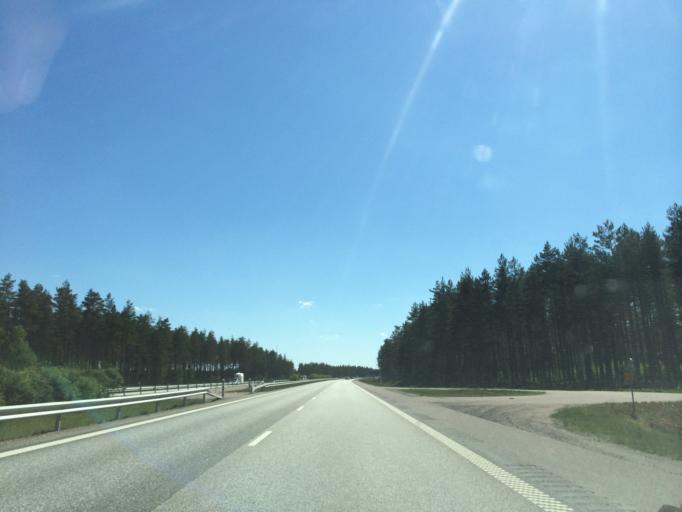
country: SE
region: Joenkoeping
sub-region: Vaggeryds Kommun
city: Vaggeryd
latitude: 57.5359
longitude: 14.1237
